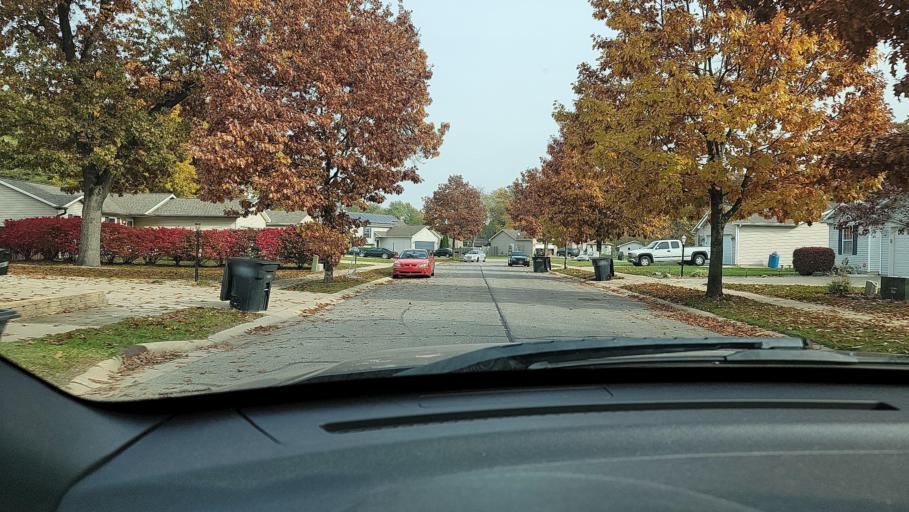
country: US
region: Indiana
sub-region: Porter County
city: Portage
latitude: 41.5910
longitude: -87.1658
